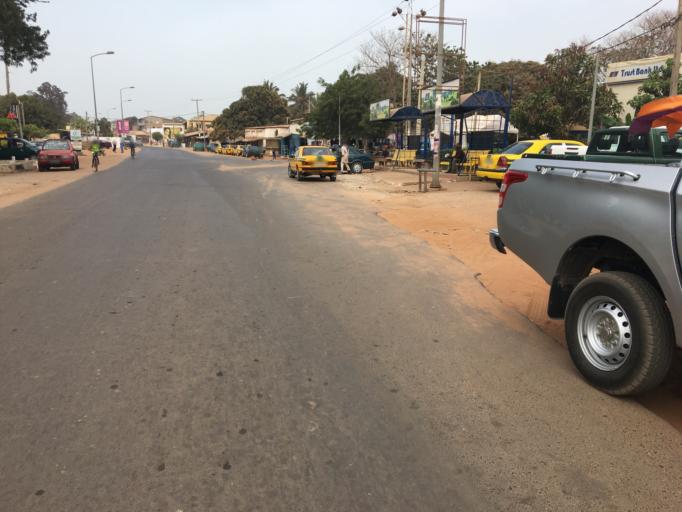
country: GM
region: Banjul
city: Bakau
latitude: 13.4803
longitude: -16.6785
